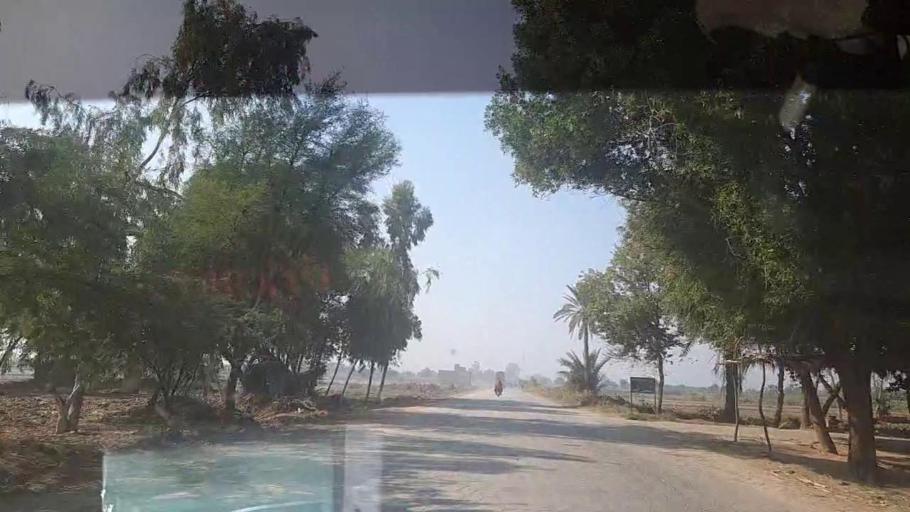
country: PK
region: Sindh
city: Kot Diji
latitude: 27.4359
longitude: 68.6422
